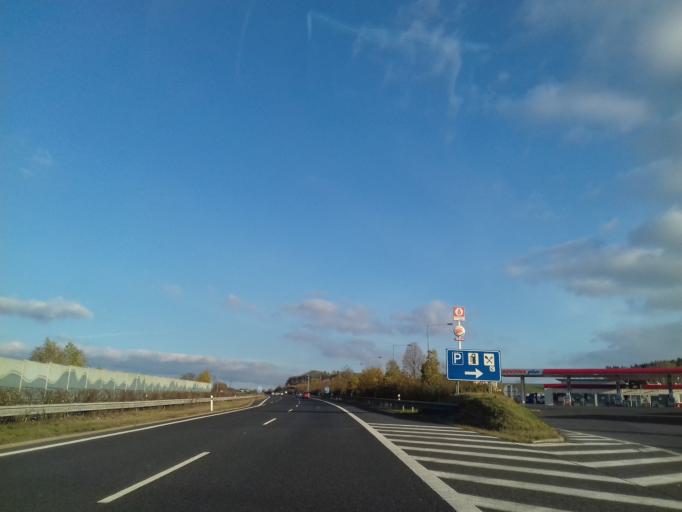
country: CZ
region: Plzensky
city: Dobrany
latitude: 49.6771
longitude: 13.3232
